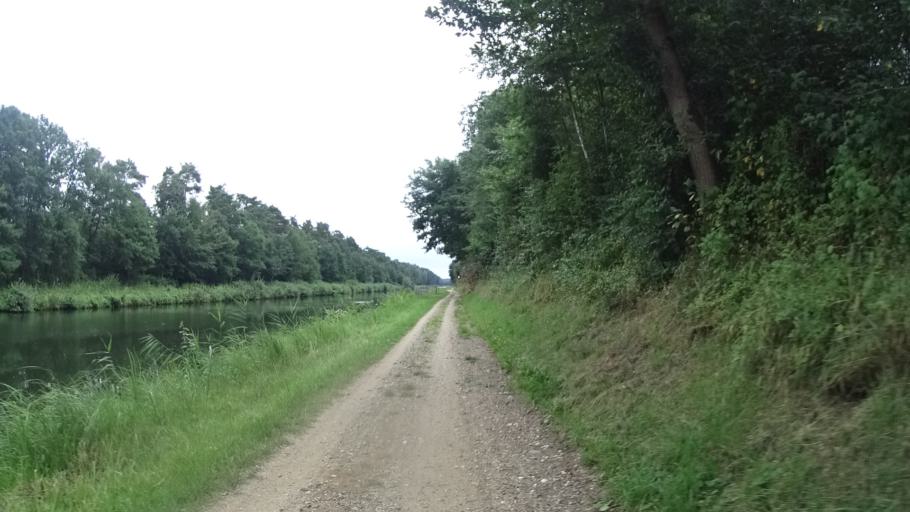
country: DE
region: Schleswig-Holstein
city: Alt Molln
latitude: 53.6030
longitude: 10.6658
